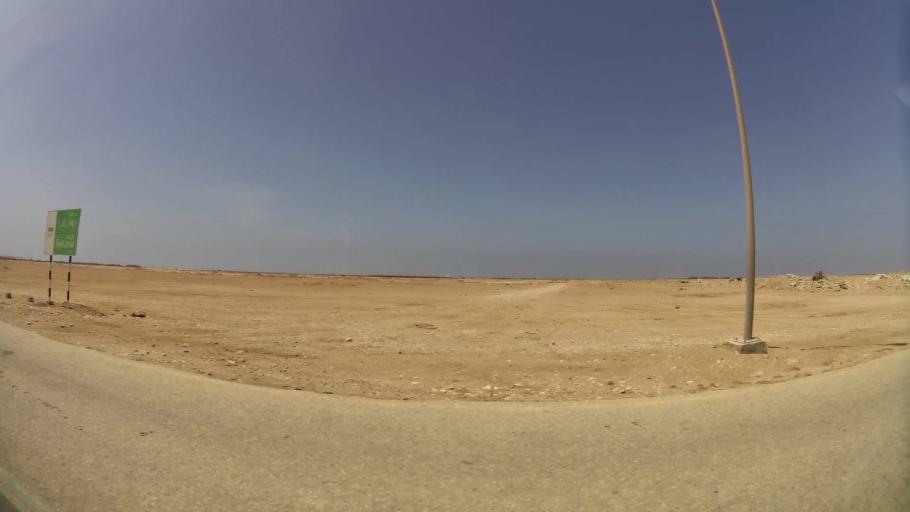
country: OM
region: Zufar
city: Salalah
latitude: 17.0379
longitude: 54.2747
